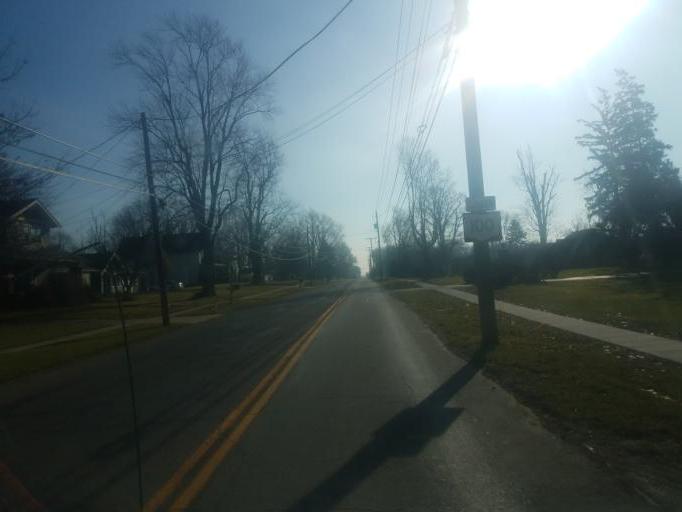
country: US
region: Ohio
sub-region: Seneca County
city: Tiffin
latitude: 41.1004
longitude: -83.1668
